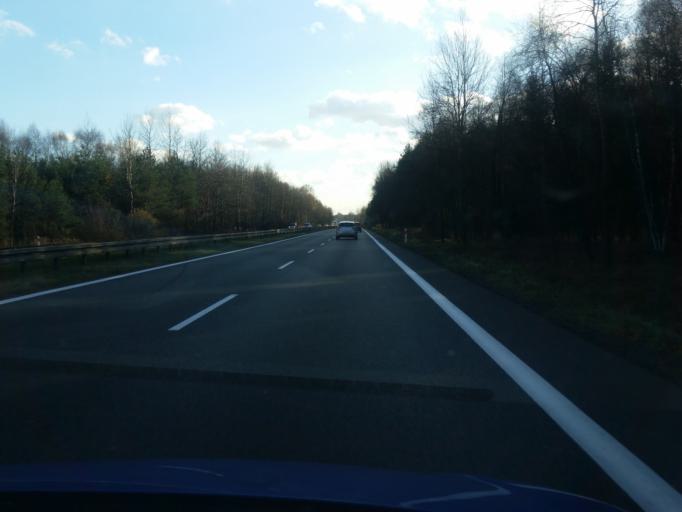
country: PL
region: Silesian Voivodeship
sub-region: Powiat bedzinski
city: Siewierz
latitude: 50.5242
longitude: 19.1926
